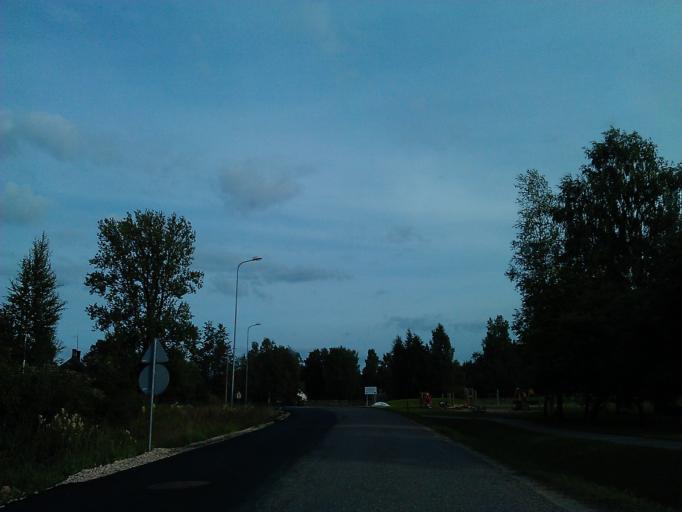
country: LV
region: Amatas Novads
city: Drabesi
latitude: 57.2054
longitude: 25.1655
